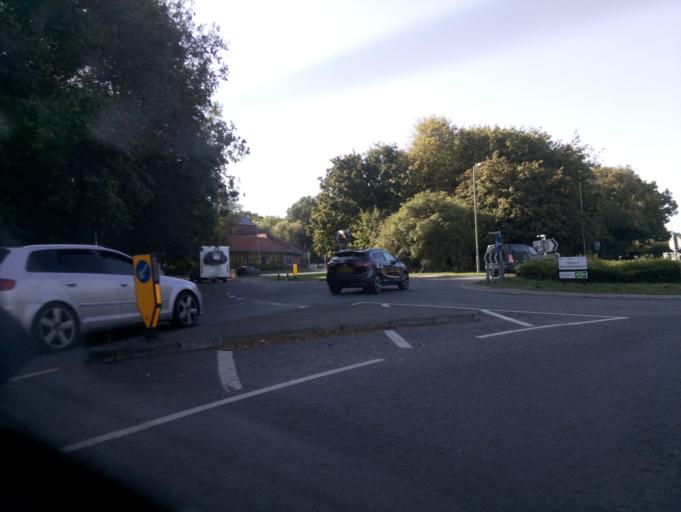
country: GB
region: England
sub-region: Hampshire
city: Tadley
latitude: 51.3486
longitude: -1.1351
